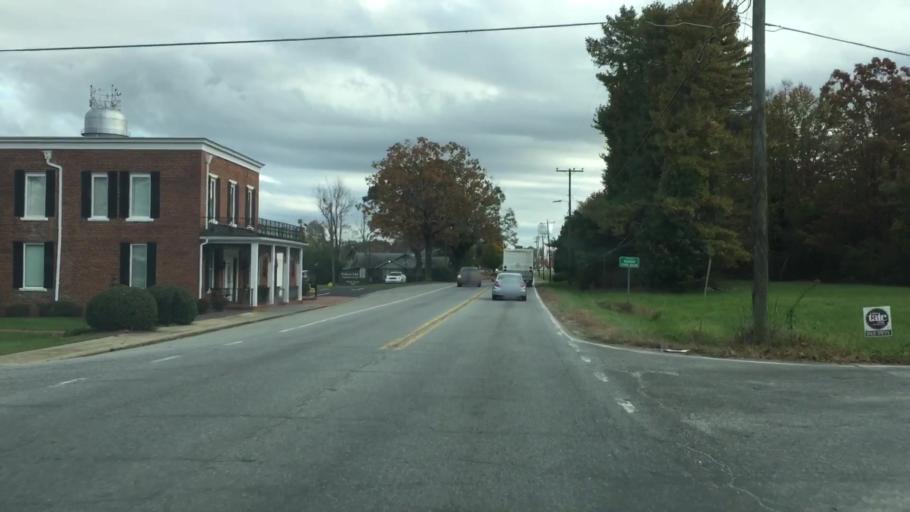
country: US
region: North Carolina
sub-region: Guilford County
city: Stokesdale
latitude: 36.2412
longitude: -79.9839
